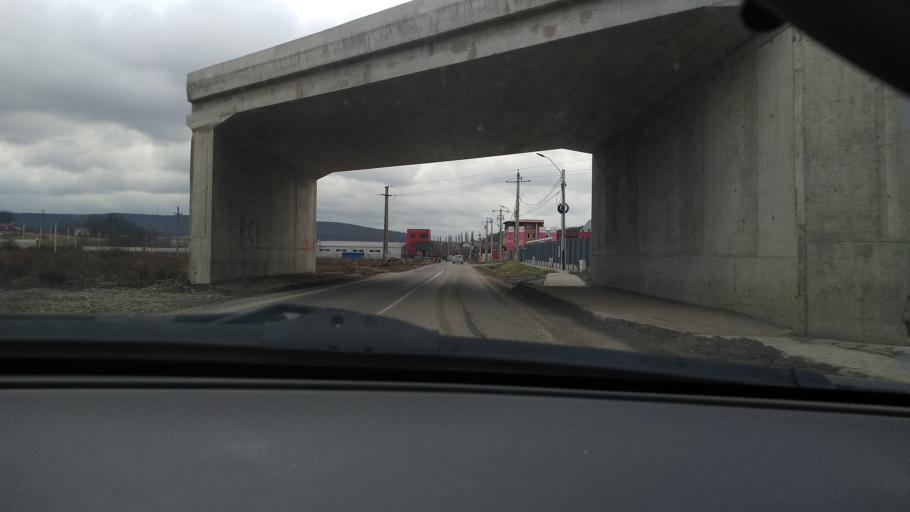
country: RO
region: Mures
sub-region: Comuna Livezeni
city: Livezeni
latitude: 46.5432
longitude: 24.6147
